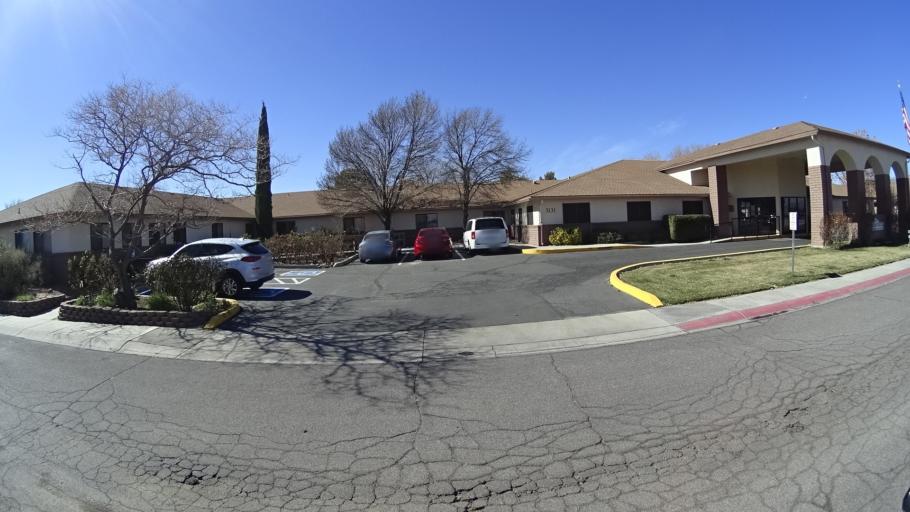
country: US
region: Arizona
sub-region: Mohave County
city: Kingman
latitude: 35.2142
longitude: -114.0401
